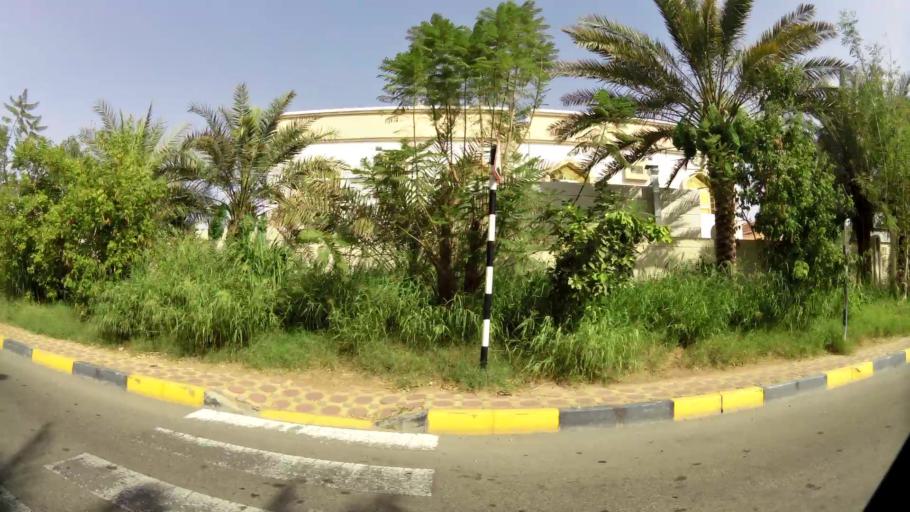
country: AE
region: Abu Dhabi
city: Al Ain
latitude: 24.2443
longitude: 55.6832
